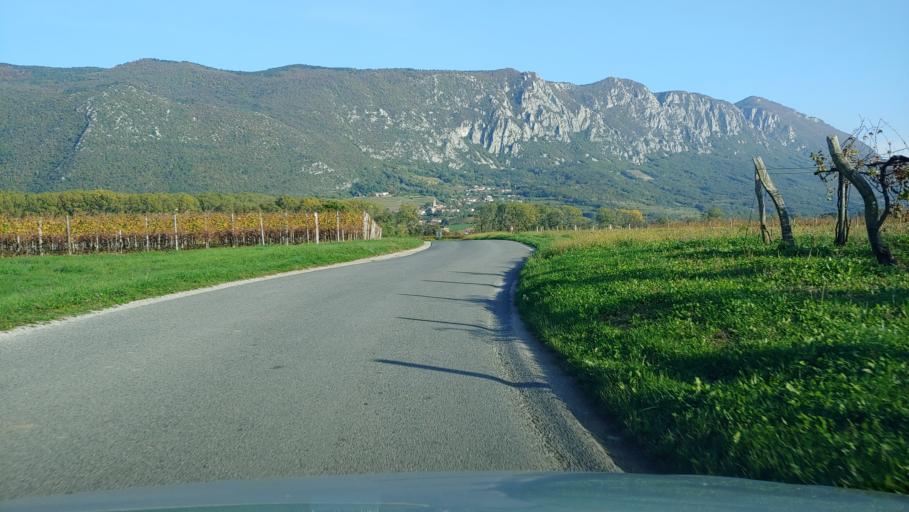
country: SI
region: Vipava
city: Vipava
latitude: 45.8402
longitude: 13.9408
